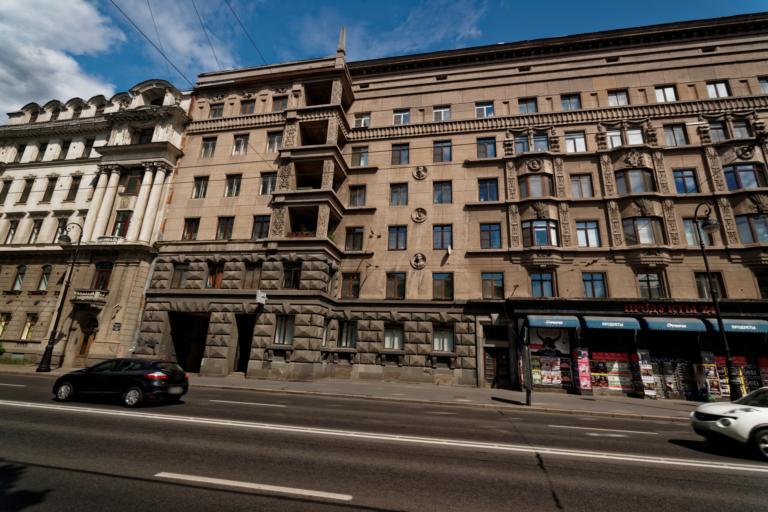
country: RU
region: Leningrad
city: Chernaya Rechka
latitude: 59.9746
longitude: 30.3038
